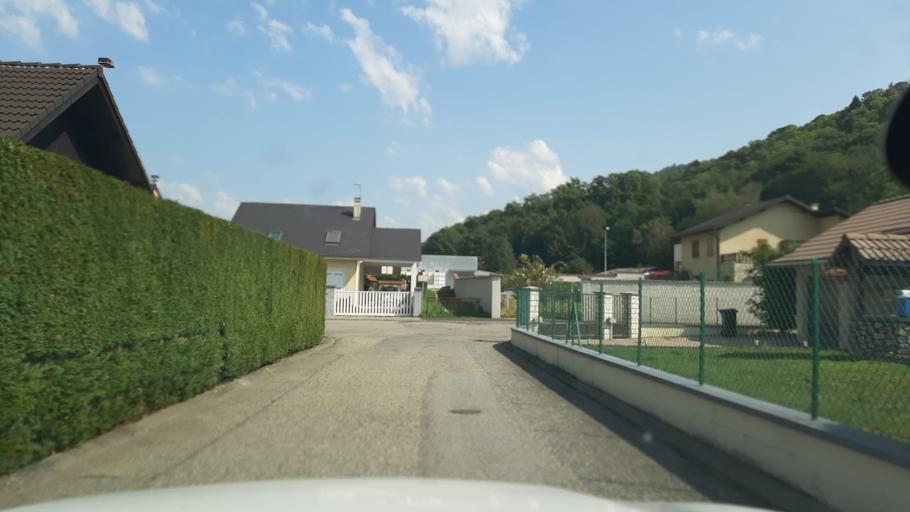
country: FR
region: Rhone-Alpes
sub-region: Departement de la Savoie
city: La Rochette
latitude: 45.4638
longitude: 6.1229
